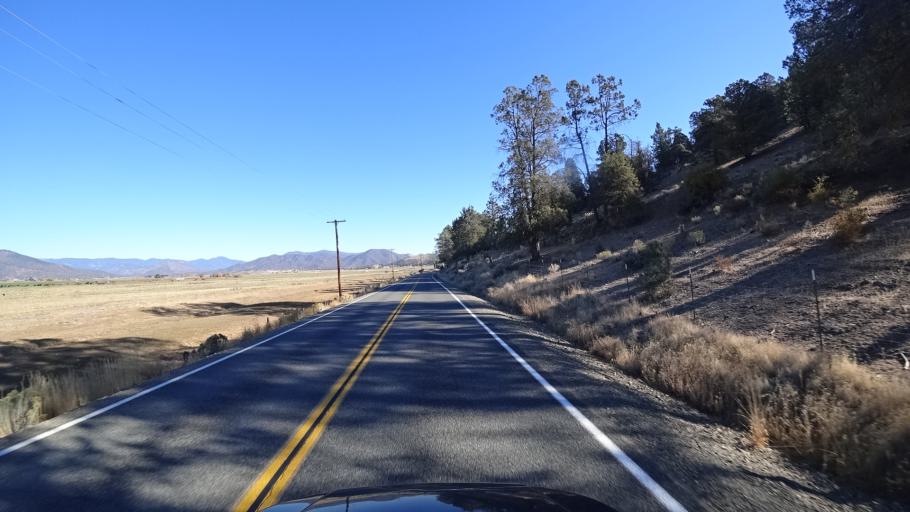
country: US
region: California
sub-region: Siskiyou County
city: Yreka
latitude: 41.5308
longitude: -122.8417
